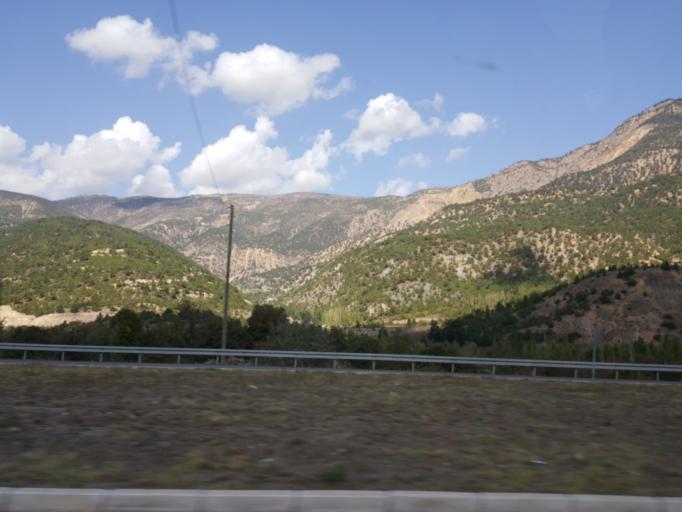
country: TR
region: Sivas
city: Dogansar
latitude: 40.3118
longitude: 37.6492
